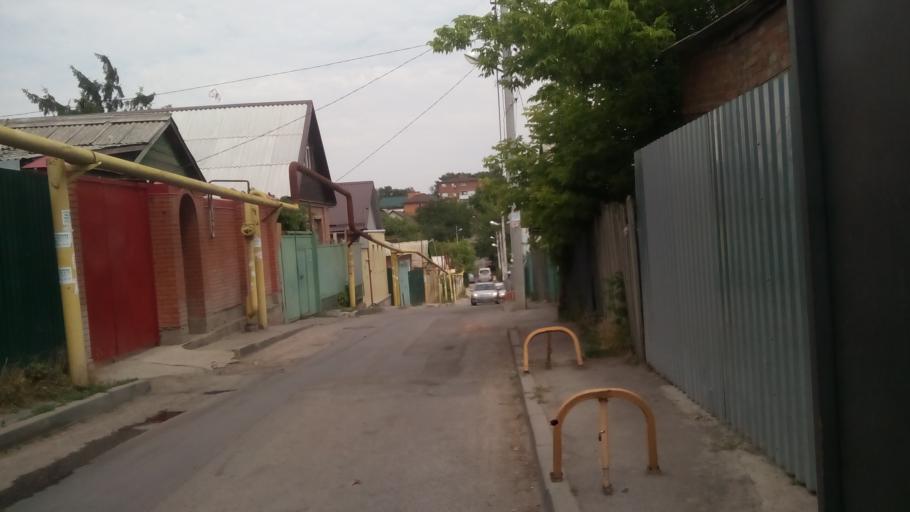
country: RU
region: Rostov
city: Rostov-na-Donu
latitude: 47.2457
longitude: 39.7428
